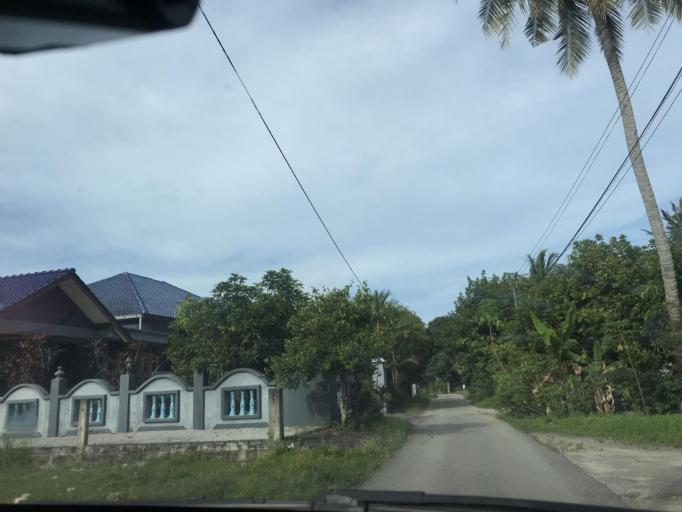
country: MY
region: Kelantan
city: Kota Bharu
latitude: 6.1326
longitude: 102.2154
